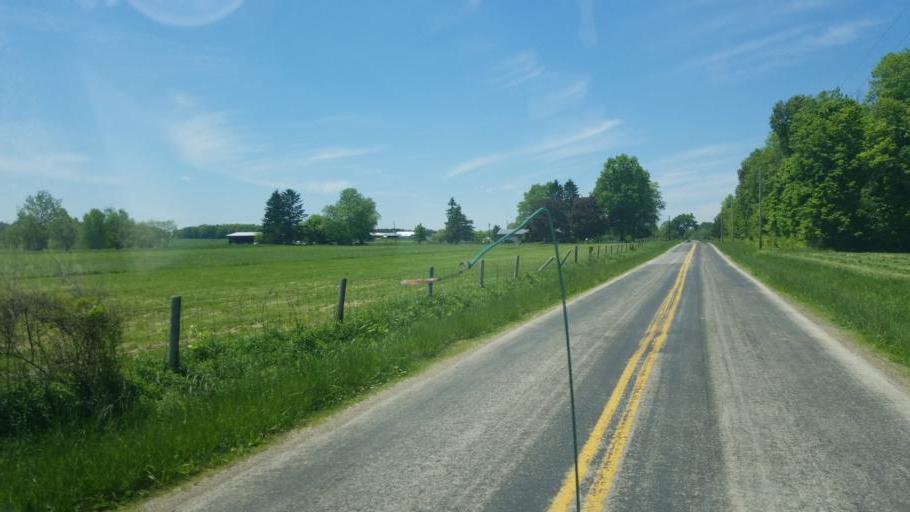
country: US
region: Ohio
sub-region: Huron County
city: New London
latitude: 40.9678
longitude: -82.4102
